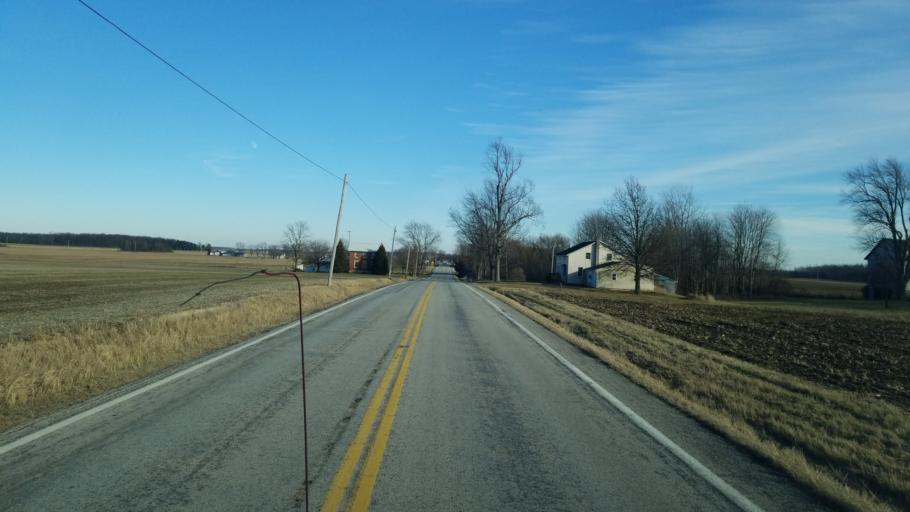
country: US
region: Ohio
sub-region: Huron County
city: Bellevue
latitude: 41.2024
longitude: -82.8314
